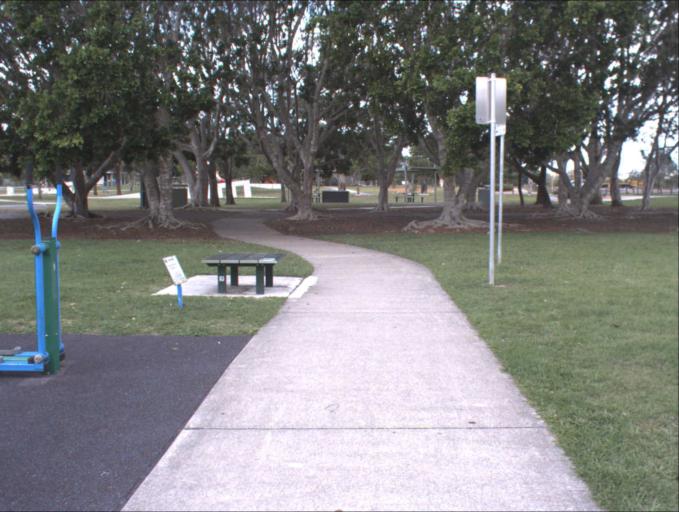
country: AU
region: Queensland
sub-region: Logan
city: Waterford West
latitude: -27.6965
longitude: 153.1328
